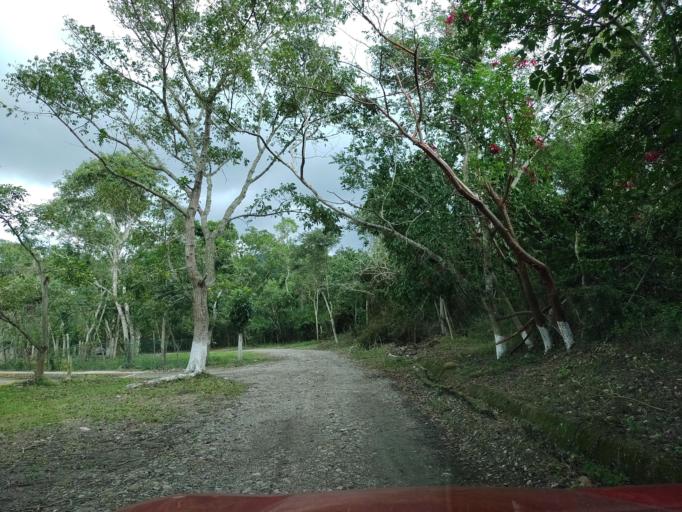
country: MX
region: Veracruz
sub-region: Papantla
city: El Chote
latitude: 20.4413
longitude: -97.3774
